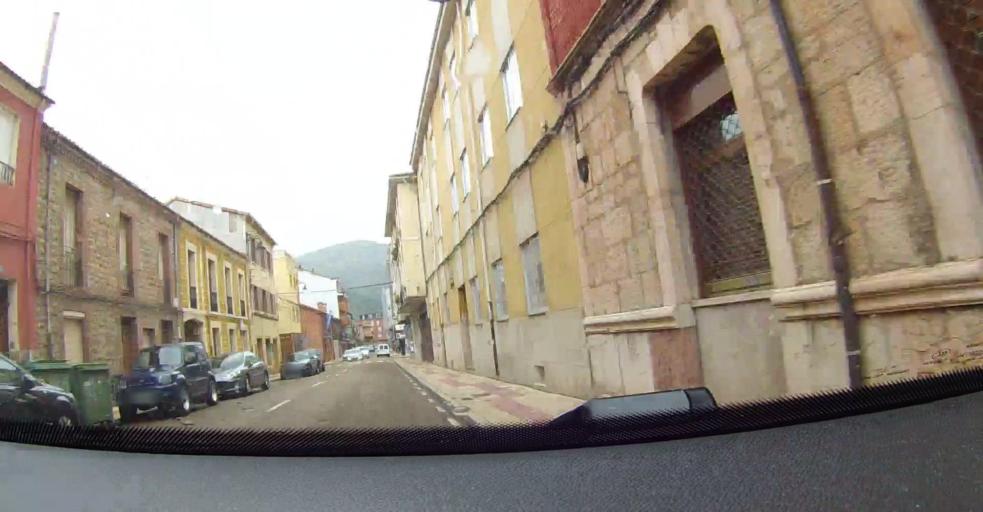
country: ES
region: Castille and Leon
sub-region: Provincia de Leon
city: Cistierna
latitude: 42.8022
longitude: -5.1268
